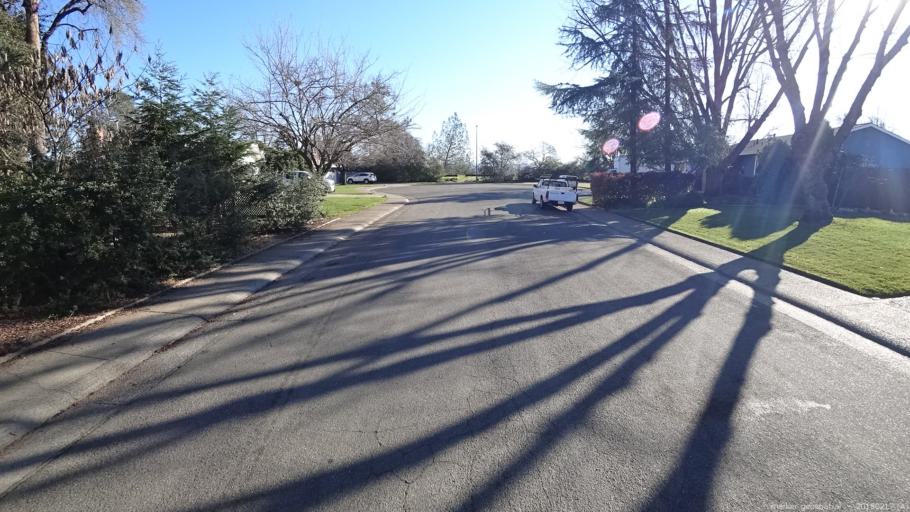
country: US
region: California
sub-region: Sacramento County
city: Folsom
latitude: 38.6746
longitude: -121.1936
